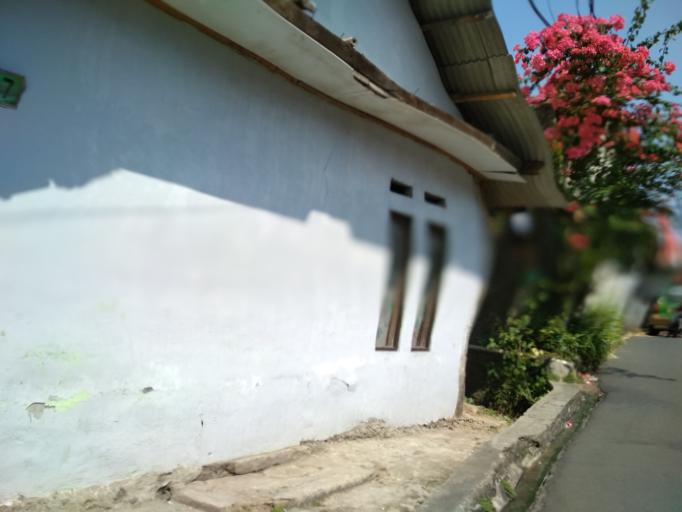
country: ID
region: West Java
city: Ciampea
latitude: -6.5552
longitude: 106.7458
